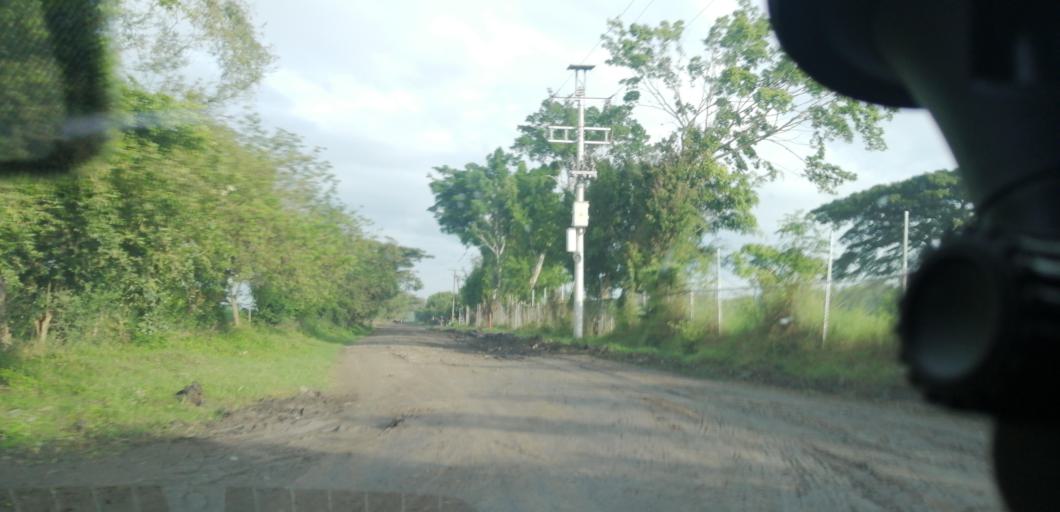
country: CO
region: Valle del Cauca
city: Palmira
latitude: 3.5425
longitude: -76.3604
